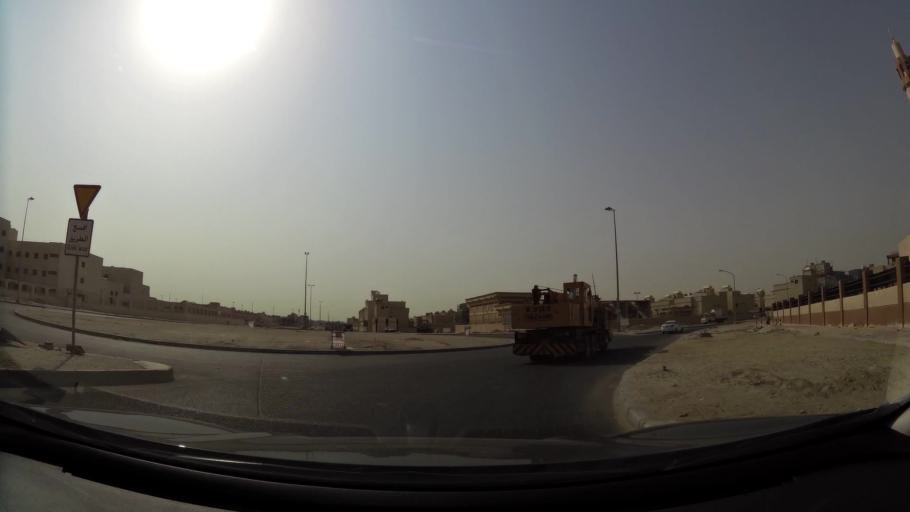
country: KW
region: Muhafazat al Jahra'
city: Al Jahra'
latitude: 29.3521
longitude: 47.7576
